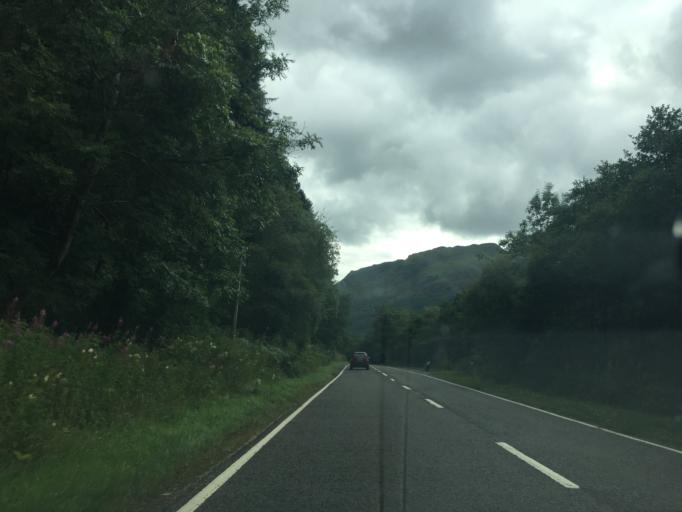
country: GB
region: Scotland
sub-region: Stirling
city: Callander
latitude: 56.3082
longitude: -4.3234
